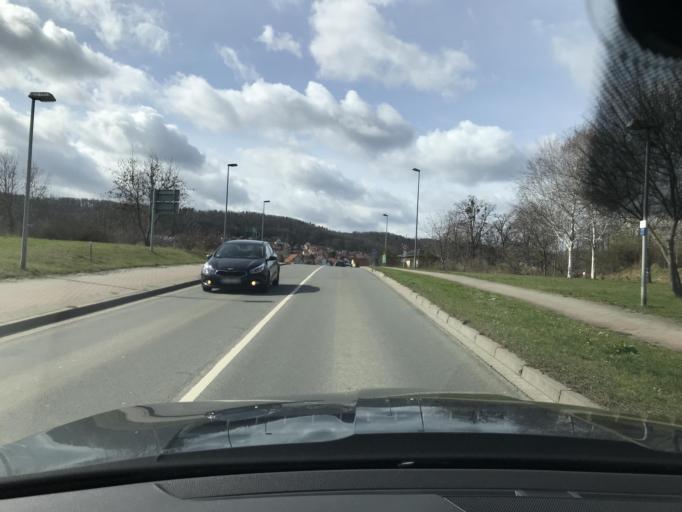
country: DE
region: Saxony-Anhalt
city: Gernrode
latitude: 51.7309
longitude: 11.1516
